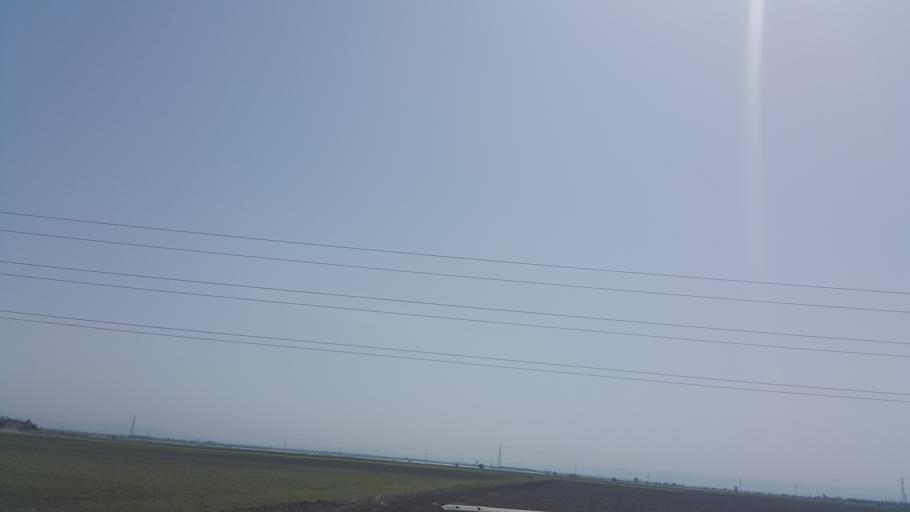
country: TR
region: Hatay
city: Serinyol
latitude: 36.3812
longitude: 36.2293
